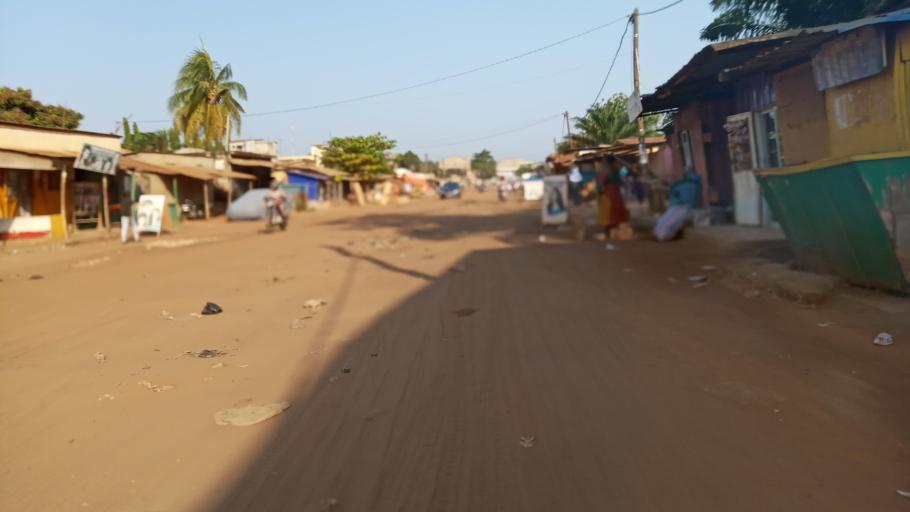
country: TG
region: Maritime
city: Lome
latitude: 6.1813
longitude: 1.1669
